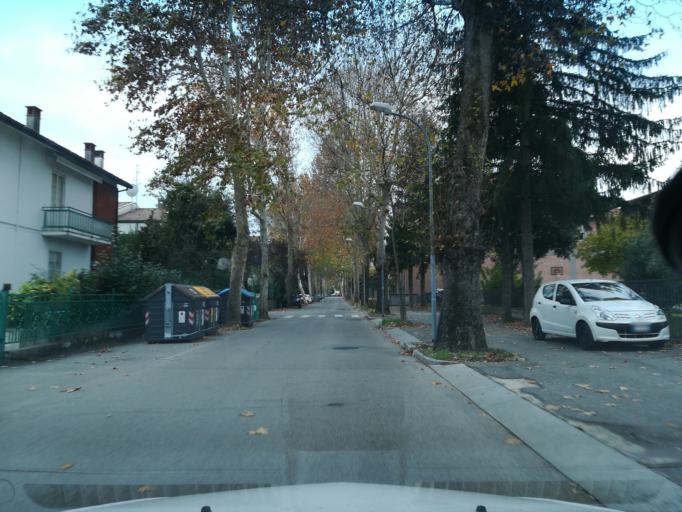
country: IT
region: Emilia-Romagna
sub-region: Provincia di Bologna
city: Imola
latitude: 44.3647
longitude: 11.6959
